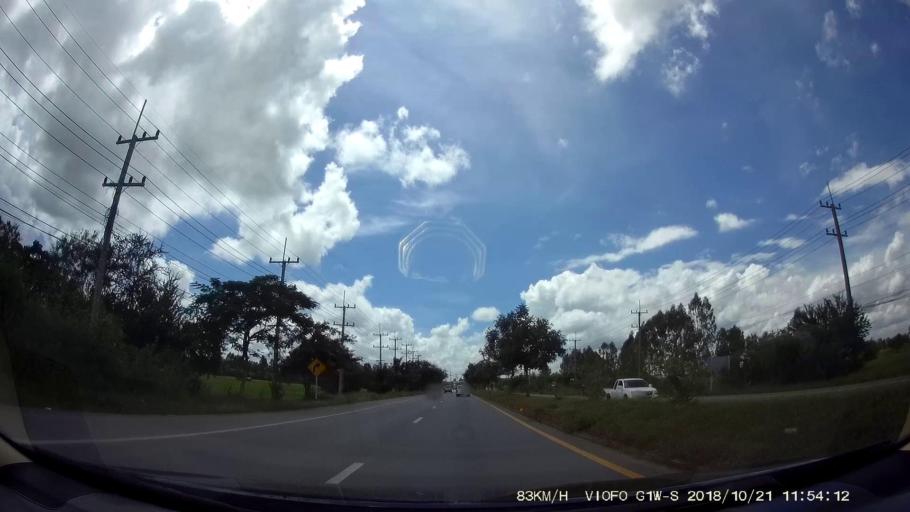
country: TH
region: Chaiyaphum
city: Chatturat
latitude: 15.5871
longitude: 101.9024
